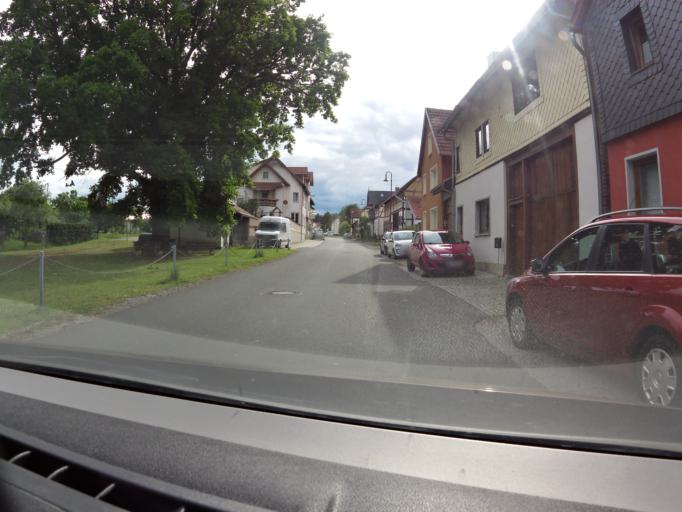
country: DE
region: Thuringia
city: Kammerforst
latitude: 51.1223
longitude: 10.4236
